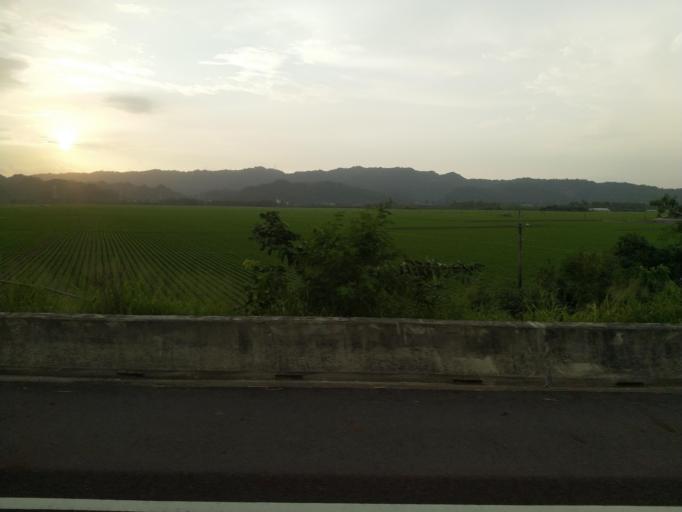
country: TW
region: Taiwan
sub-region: Pingtung
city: Pingtung
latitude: 22.8247
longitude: 120.4878
